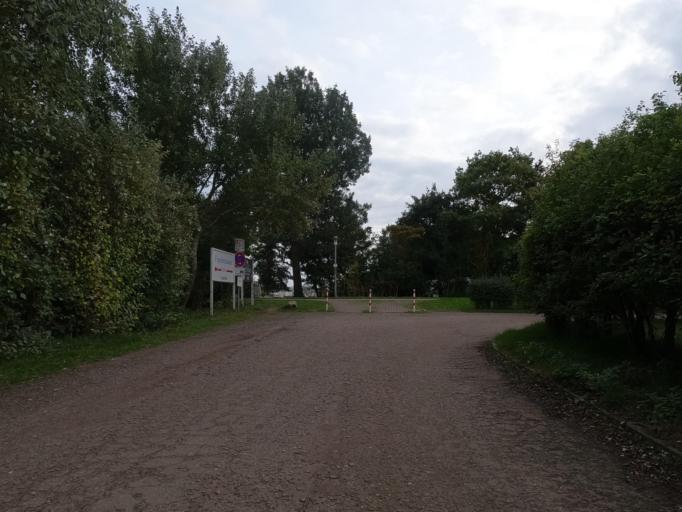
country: DE
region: Schleswig-Holstein
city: Neukirchen
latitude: 54.3250
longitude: 11.0713
